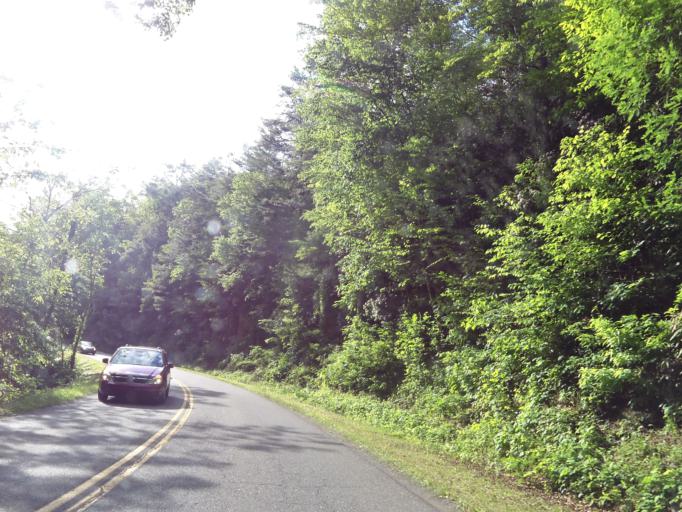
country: US
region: Tennessee
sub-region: Sevier County
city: Gatlinburg
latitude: 35.6631
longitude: -83.6078
